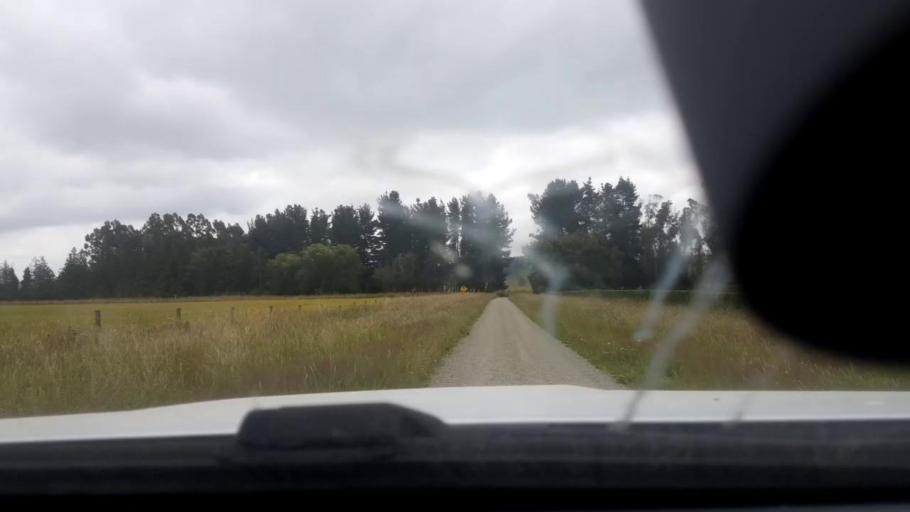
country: NZ
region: Canterbury
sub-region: Timaru District
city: Pleasant Point
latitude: -44.2219
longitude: 171.1630
